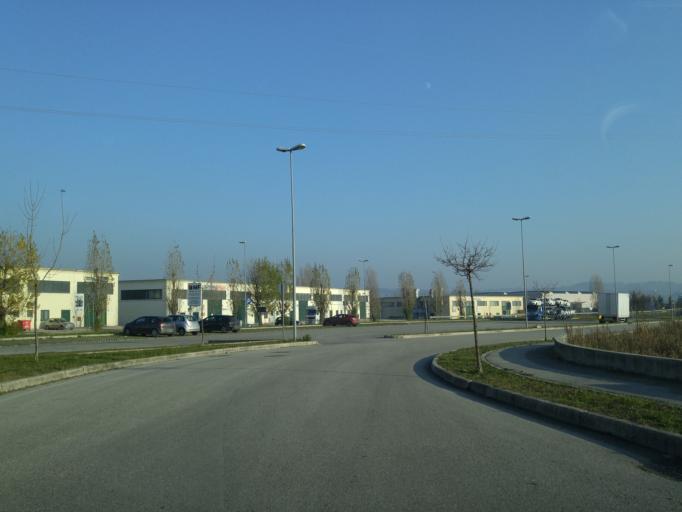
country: IT
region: The Marches
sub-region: Provincia di Pesaro e Urbino
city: Lucrezia
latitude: 43.7712
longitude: 12.9554
